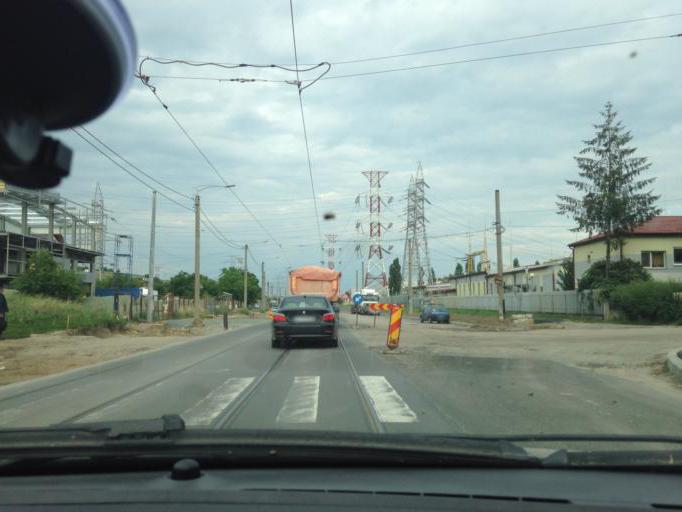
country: RO
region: Cluj
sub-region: Municipiul Cluj-Napoca
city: Cluj-Napoca
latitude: 46.7961
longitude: 23.6370
